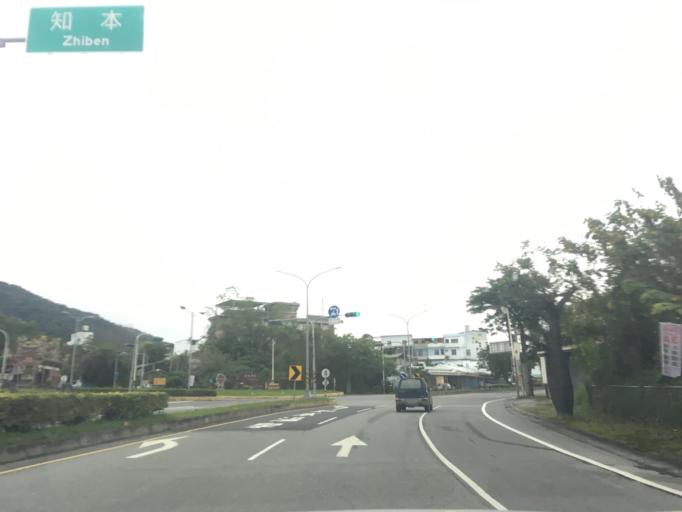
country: TW
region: Taiwan
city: Taitung City
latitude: 22.7038
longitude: 121.0399
